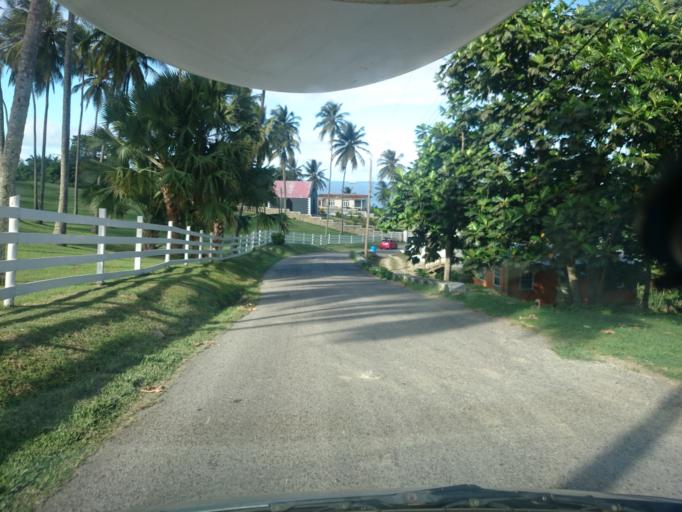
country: BB
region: Saint Joseph
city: Bathsheba
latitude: 13.2122
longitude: -59.5273
